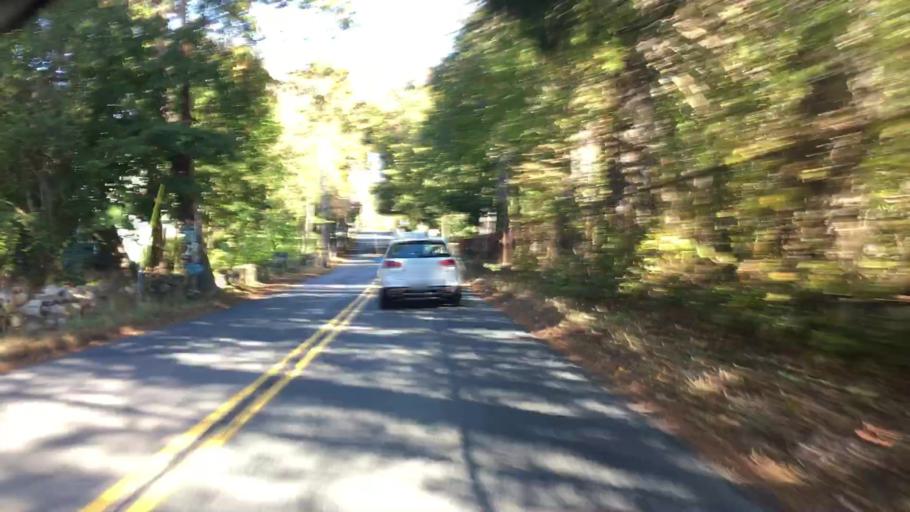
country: US
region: Massachusetts
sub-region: Middlesex County
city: Framingham Center
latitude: 42.2865
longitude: -71.4598
